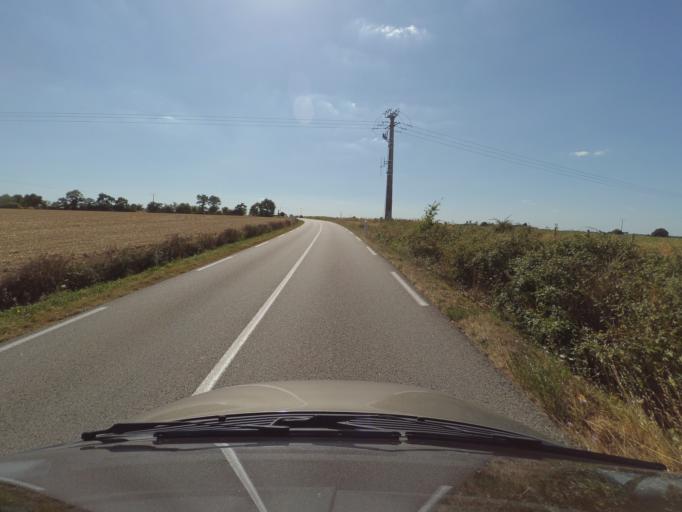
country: FR
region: Pays de la Loire
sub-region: Departement de la Vendee
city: Tiffauges
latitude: 47.0088
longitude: -1.1340
